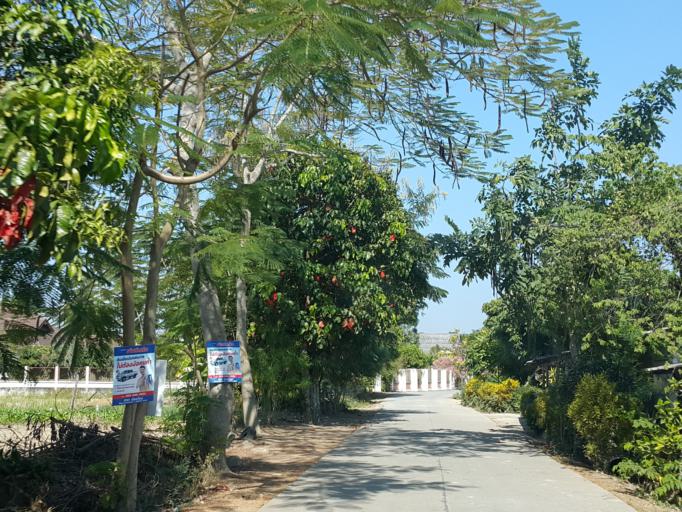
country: TH
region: Chiang Mai
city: San Sai
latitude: 18.9571
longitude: 98.9877
